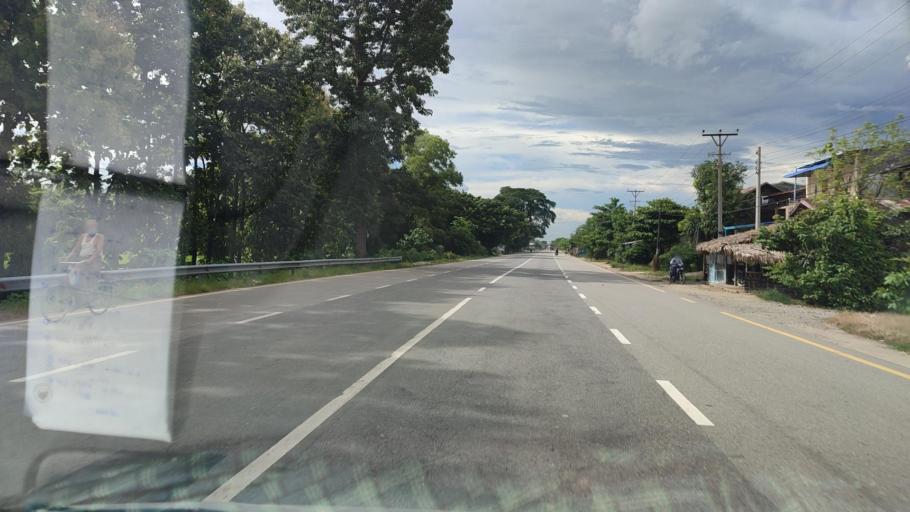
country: MM
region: Bago
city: Pyu
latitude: 18.5325
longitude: 96.4319
